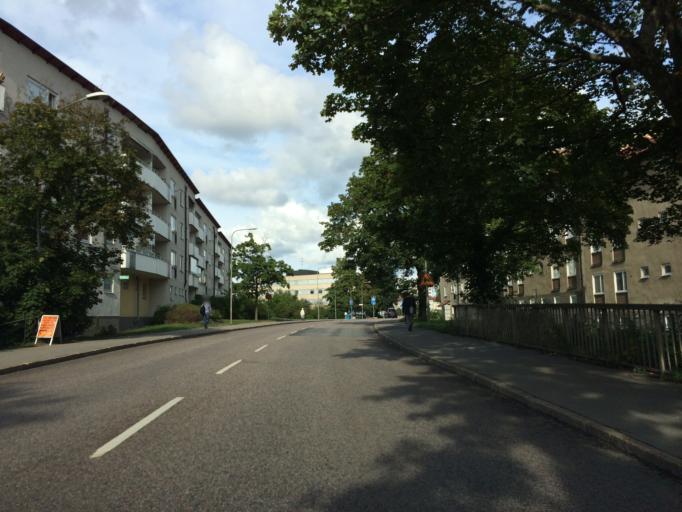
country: SE
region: Stockholm
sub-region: Huddinge Kommun
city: Segeltorp
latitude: 59.2848
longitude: 17.9602
